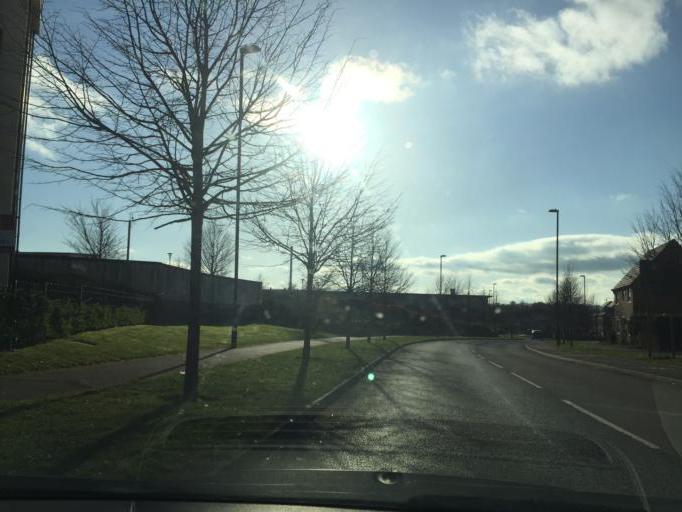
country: GB
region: England
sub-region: Coventry
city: Coventry
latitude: 52.3981
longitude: -1.4820
